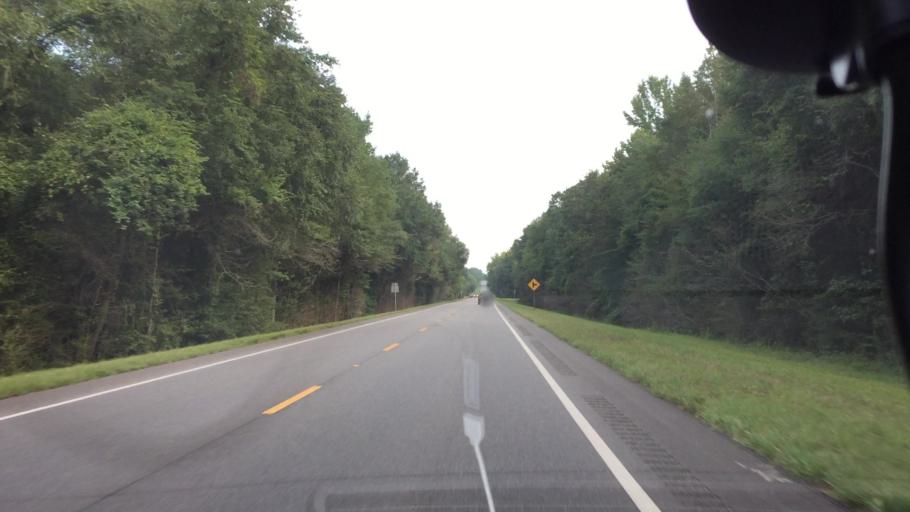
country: US
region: Alabama
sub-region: Pike County
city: Brundidge
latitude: 31.5918
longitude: -85.9431
